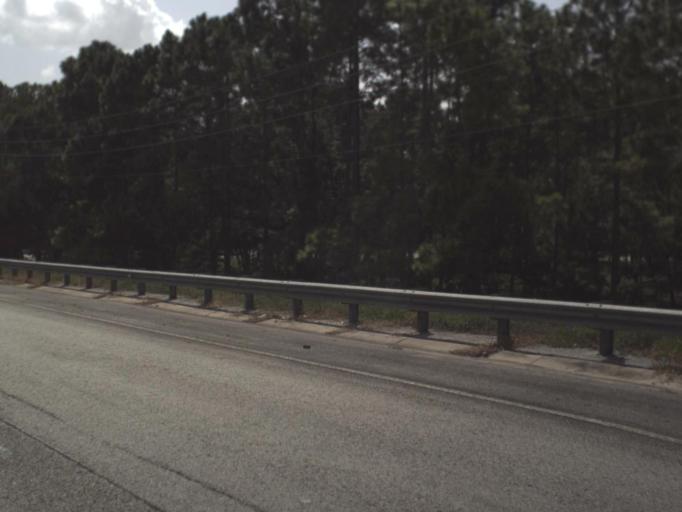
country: US
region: Florida
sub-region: Polk County
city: Haines City
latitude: 28.1061
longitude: -81.6433
